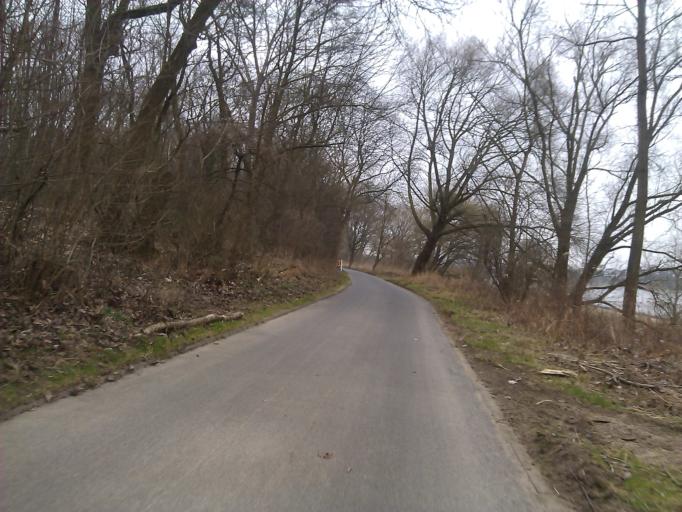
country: DE
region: North Rhine-Westphalia
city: Niederkassel
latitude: 50.8201
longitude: 7.0180
